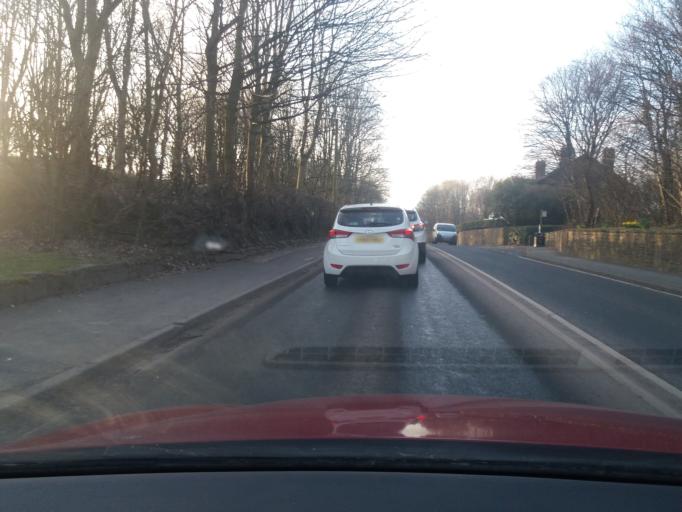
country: GB
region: England
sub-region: Lancashire
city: Euxton
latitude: 53.6566
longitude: -2.6546
